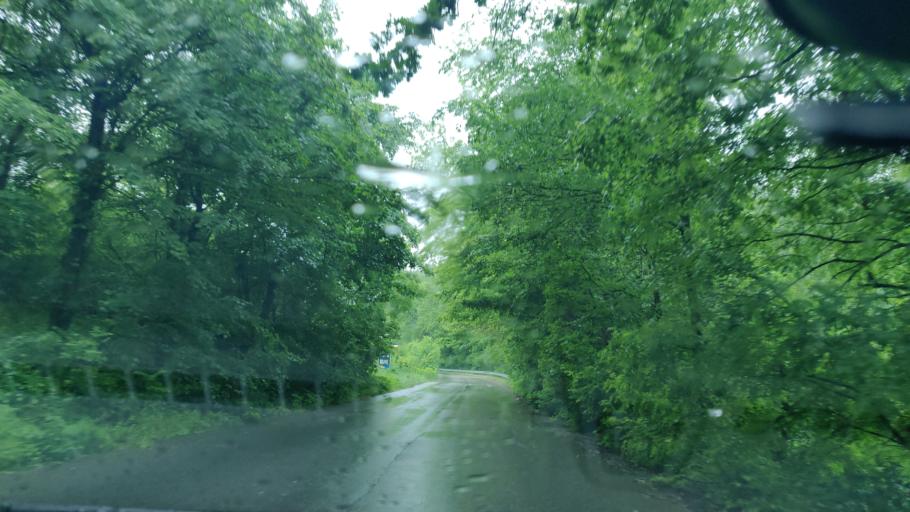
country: RO
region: Giurgiu
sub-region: Comuna Bulbucata
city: Bulbucata
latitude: 44.2889
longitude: 25.7790
